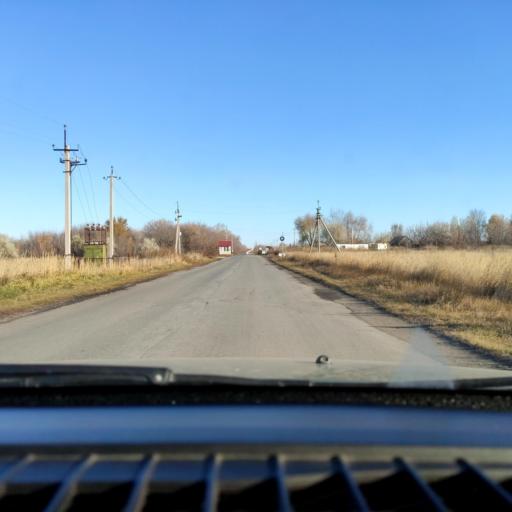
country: RU
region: Samara
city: Tol'yatti
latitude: 53.6583
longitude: 49.3321
